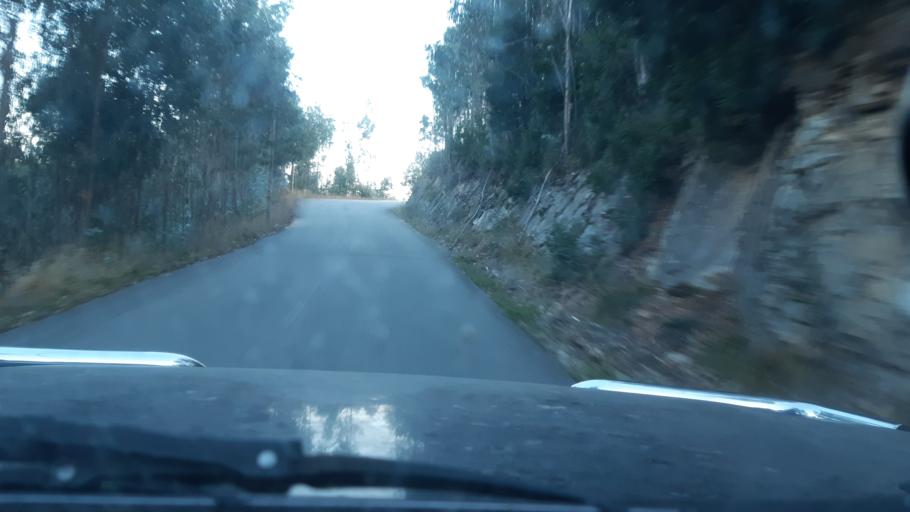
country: PT
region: Aveiro
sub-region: Agueda
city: Aguada de Cima
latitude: 40.5672
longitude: -8.3619
